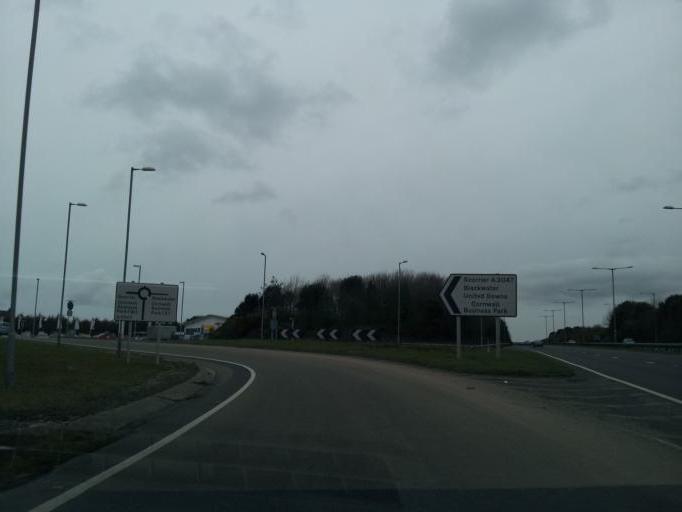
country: GB
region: England
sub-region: Cornwall
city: St. Day
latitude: 50.2569
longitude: -5.1956
